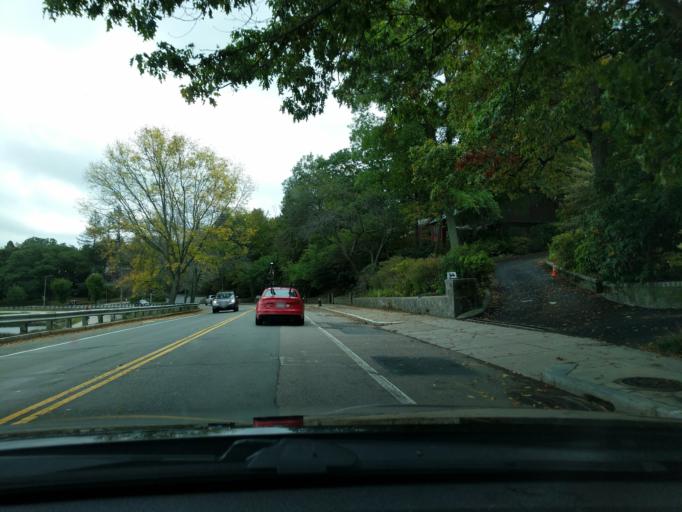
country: US
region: Massachusetts
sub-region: Norfolk County
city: Brookline
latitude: 42.3324
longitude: -71.1590
